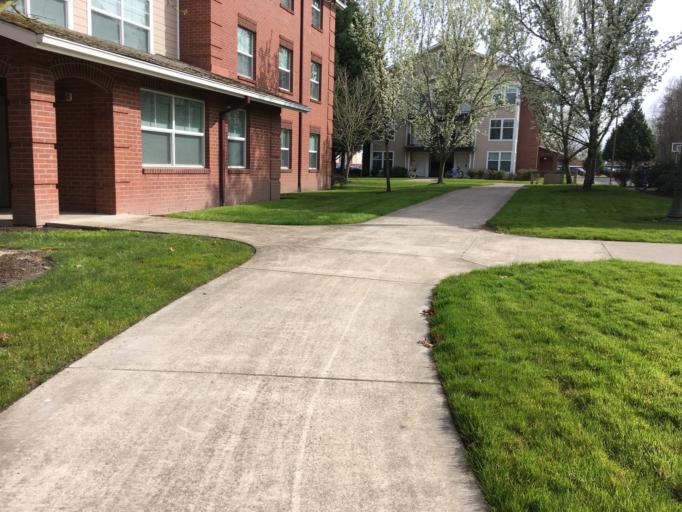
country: US
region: Oregon
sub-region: Yamhill County
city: McMinnville
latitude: 45.1974
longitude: -123.1990
